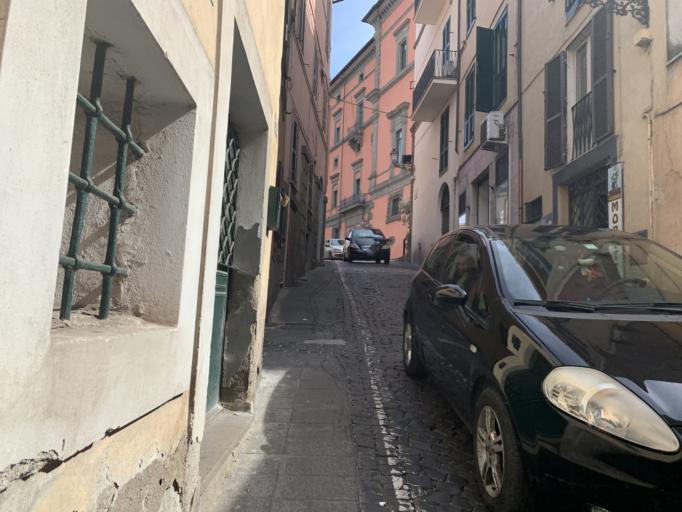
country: IT
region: Latium
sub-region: Citta metropolitana di Roma Capitale
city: Castel Gandolfo
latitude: 41.7703
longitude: 12.6584
